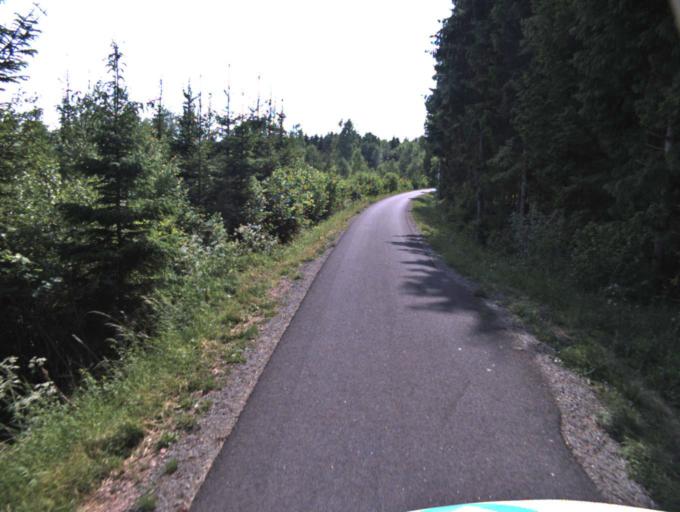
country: SE
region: Skane
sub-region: Kristianstads Kommun
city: Tollarp
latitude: 56.1981
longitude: 14.2801
